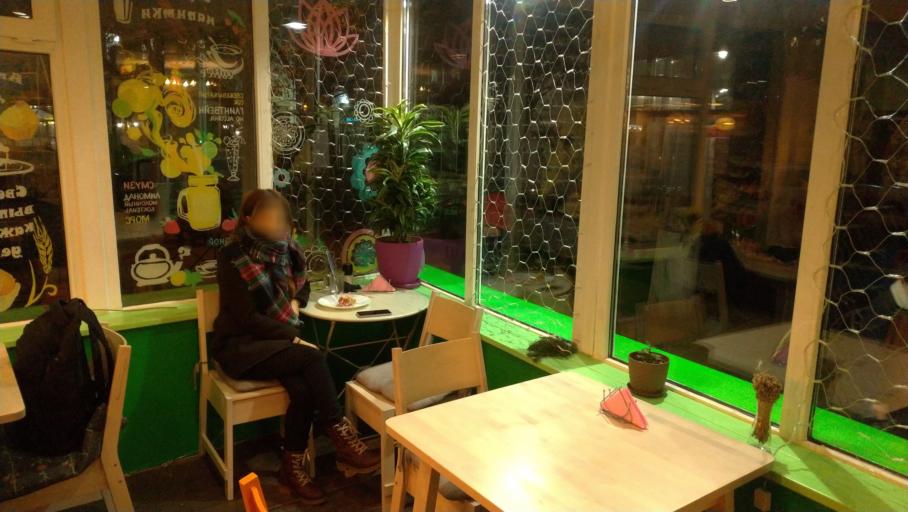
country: RU
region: Krasnodarskiy
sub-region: Sochi City
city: Sochi
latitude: 43.5846
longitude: 39.7202
